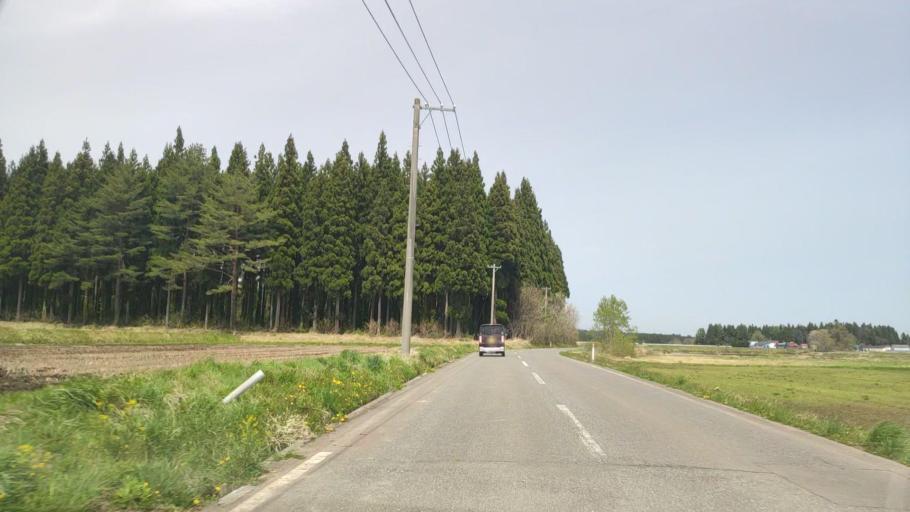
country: JP
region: Aomori
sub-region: Misawa Shi
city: Inuotose
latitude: 40.7680
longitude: 141.1214
